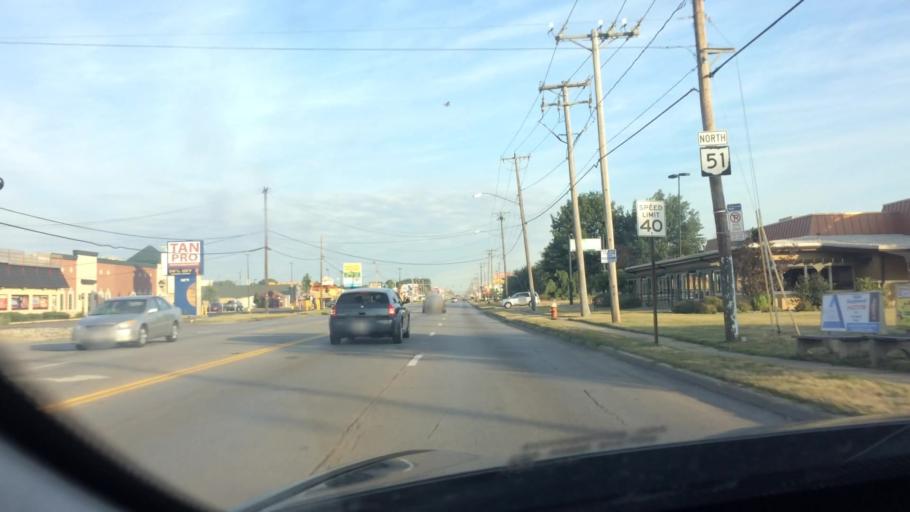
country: US
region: Ohio
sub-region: Lucas County
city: Ottawa Hills
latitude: 41.6995
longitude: -83.6456
